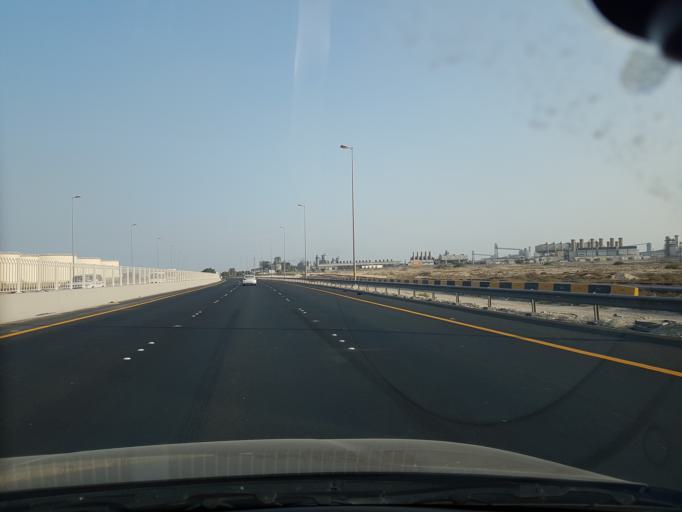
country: BH
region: Northern
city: Ar Rifa'
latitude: 26.1035
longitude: 50.6020
